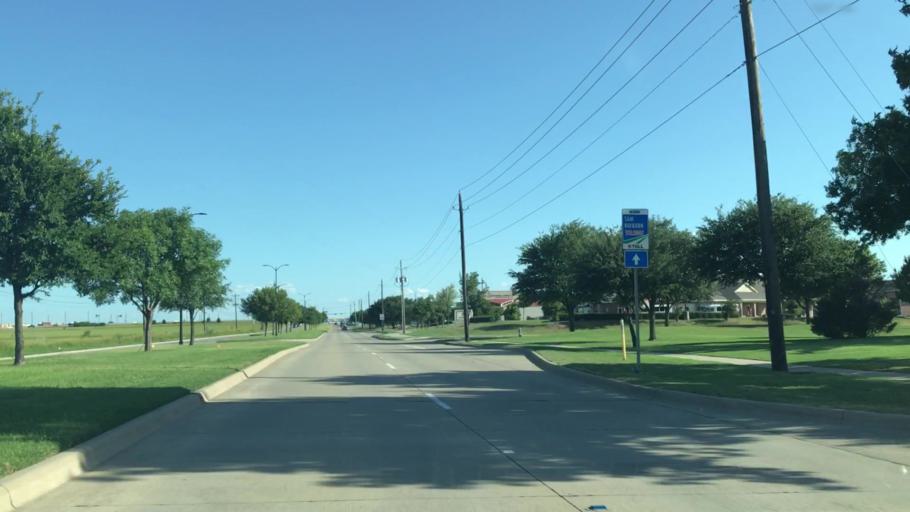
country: US
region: Texas
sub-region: Collin County
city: Frisco
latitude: 33.1206
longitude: -96.7681
